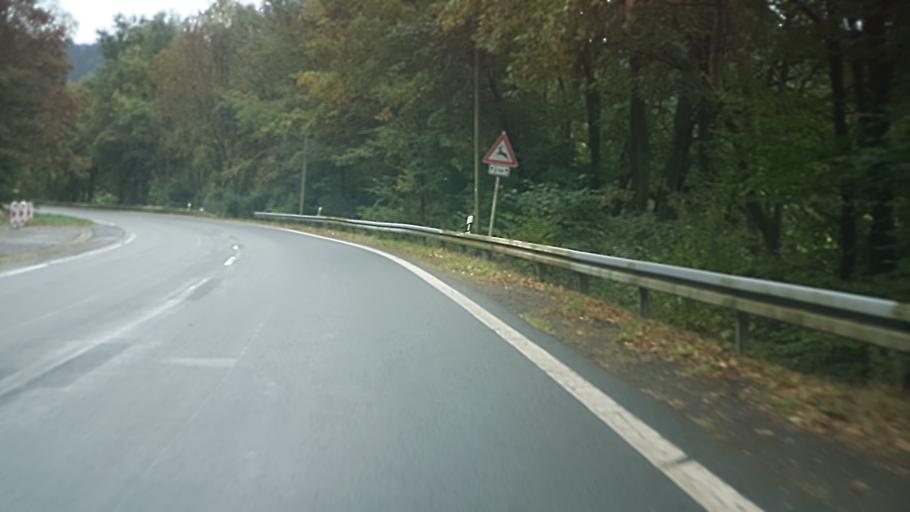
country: DE
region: North Rhine-Westphalia
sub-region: Regierungsbezirk Arnsberg
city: Herscheid
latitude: 51.1533
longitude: 7.7094
